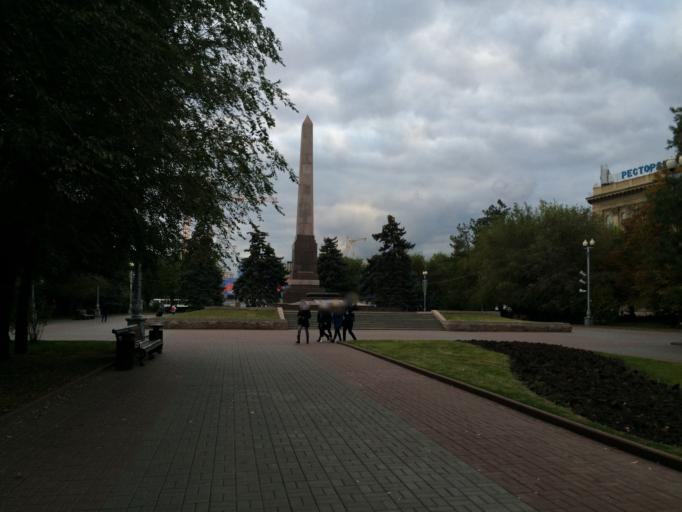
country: RU
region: Volgograd
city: Volgograd
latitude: 48.7078
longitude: 44.5158
